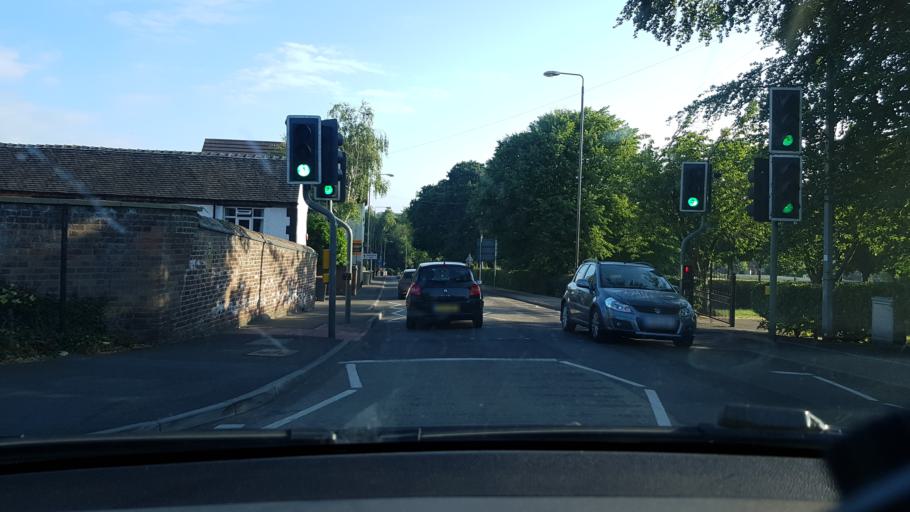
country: GB
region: England
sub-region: Nottinghamshire
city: Eastwood
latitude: 53.0200
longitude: -1.3079
